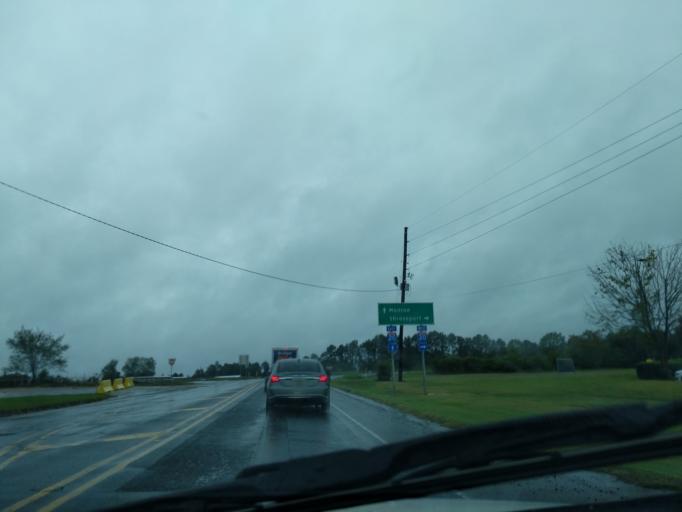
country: US
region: Louisiana
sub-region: Webster Parish
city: Minden
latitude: 32.5821
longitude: -93.2479
